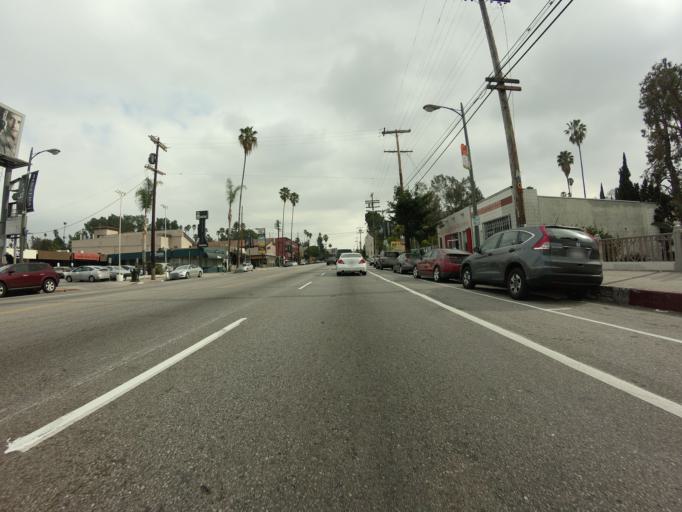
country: US
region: California
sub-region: Los Angeles County
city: Silver Lake
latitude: 34.0825
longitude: -118.2728
